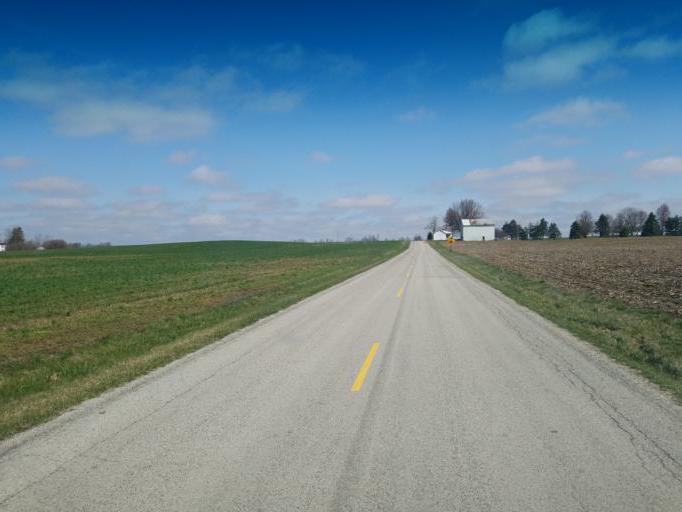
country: US
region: Ohio
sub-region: Crawford County
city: Bucyrus
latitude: 40.8968
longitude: -82.9401
